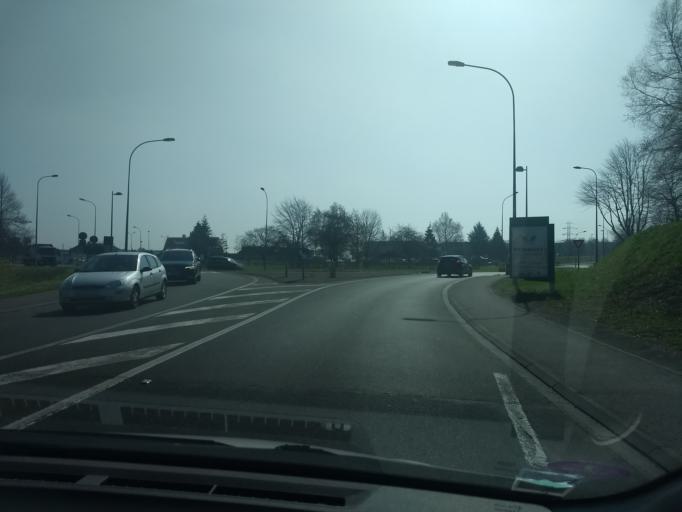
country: FR
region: Nord-Pas-de-Calais
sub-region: Departement du Pas-de-Calais
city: Saint-Omer
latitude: 50.7416
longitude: 2.2575
